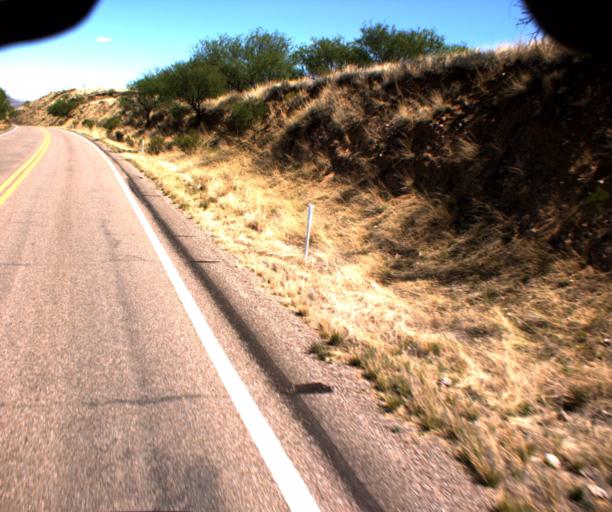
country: US
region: Arizona
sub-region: Santa Cruz County
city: Rio Rico
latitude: 31.4669
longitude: -110.8219
